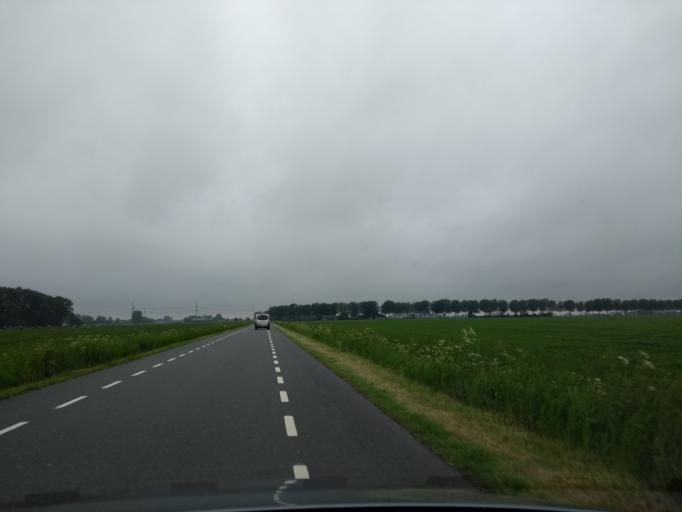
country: NL
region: Groningen
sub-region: Gemeente Zuidhorn
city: Aduard
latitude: 53.2599
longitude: 6.4971
